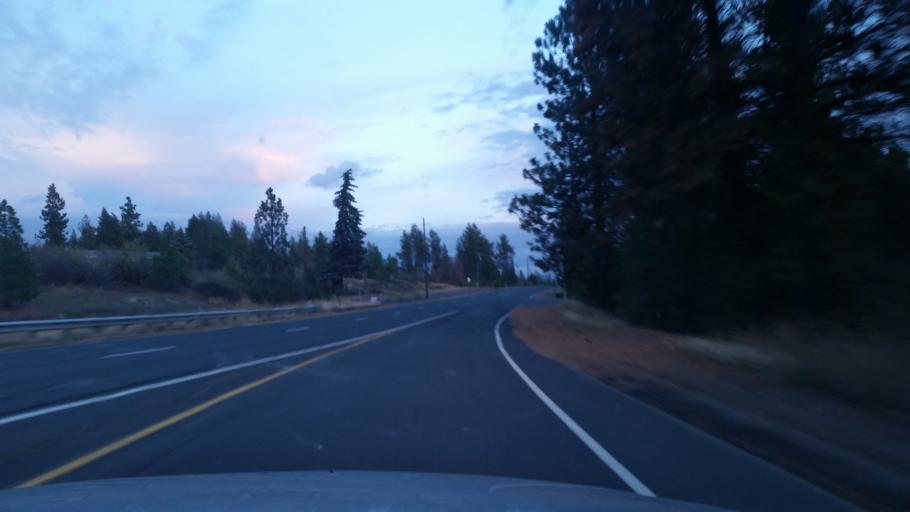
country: US
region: Washington
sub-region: Spokane County
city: Spokane
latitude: 47.6419
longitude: -117.4823
